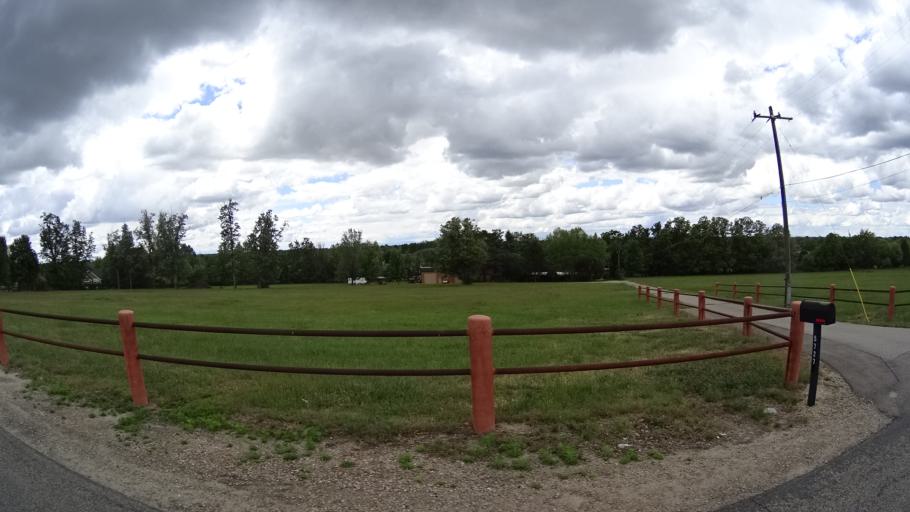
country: US
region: Idaho
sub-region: Ada County
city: Garden City
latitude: 43.6745
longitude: -116.2604
